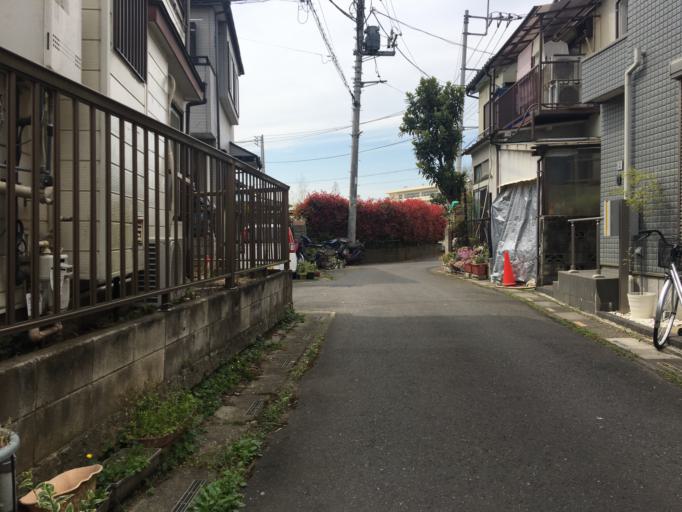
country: JP
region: Saitama
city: Shiki
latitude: 35.8487
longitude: 139.5599
